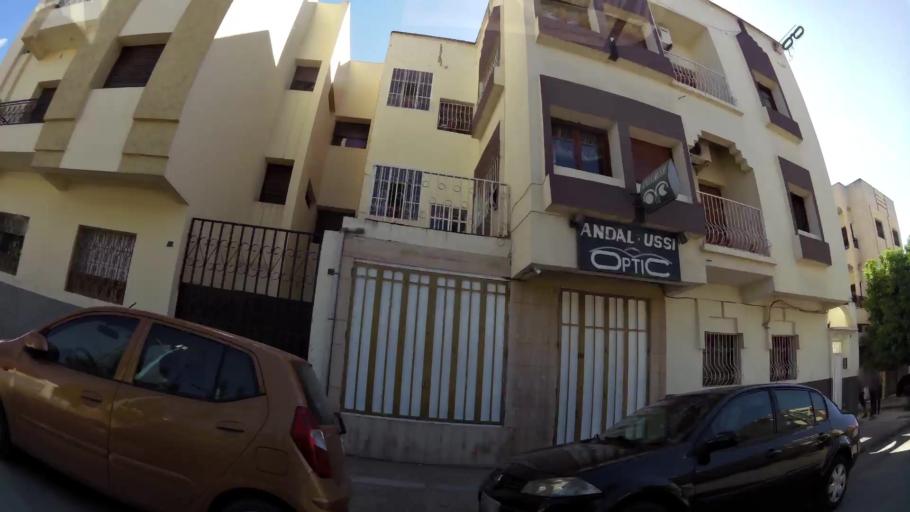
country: MA
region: Fes-Boulemane
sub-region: Fes
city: Fes
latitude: 34.0188
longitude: -4.9763
